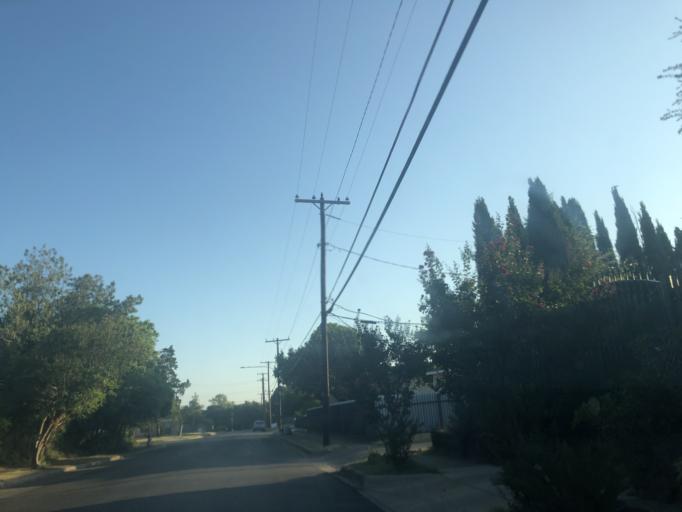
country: US
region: Texas
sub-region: Dallas County
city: Dallas
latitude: 32.7506
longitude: -96.8338
